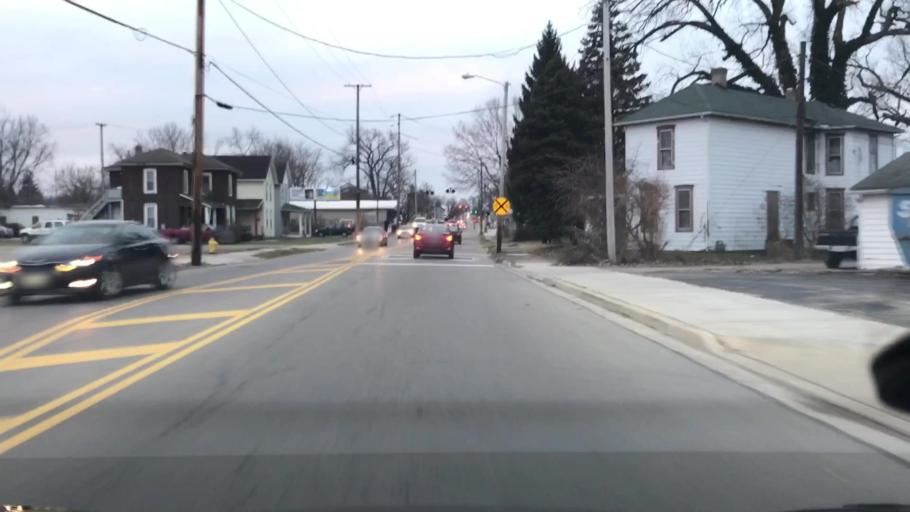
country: US
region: Ohio
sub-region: Clark County
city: Springfield
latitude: 39.9363
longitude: -83.7782
